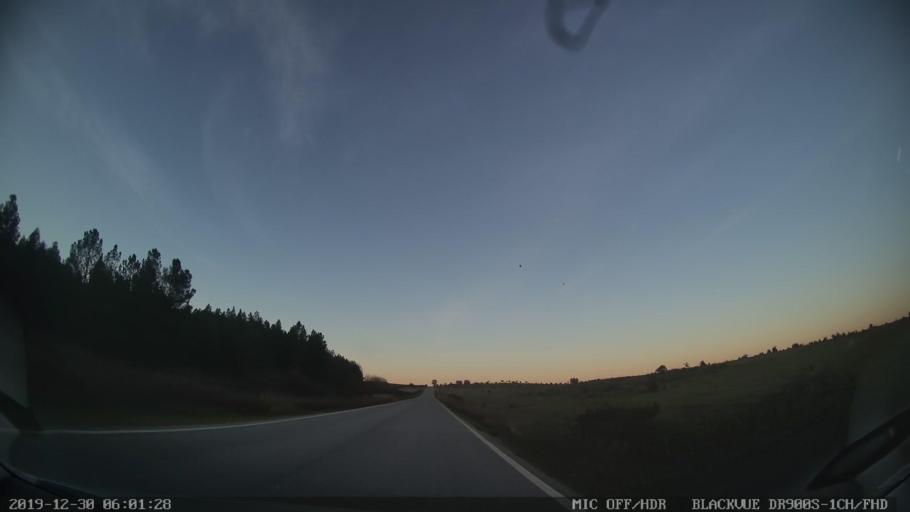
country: PT
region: Castelo Branco
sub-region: Penamacor
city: Penamacor
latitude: 40.0609
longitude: -7.2434
